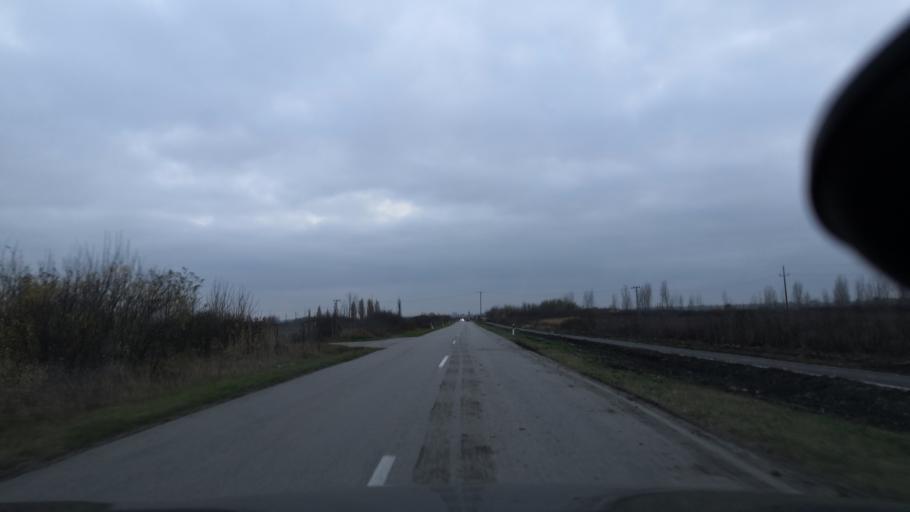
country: RS
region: Autonomna Pokrajina Vojvodina
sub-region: Severnobanatski Okrug
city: Novi Knezevac
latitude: 46.0811
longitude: 20.1054
